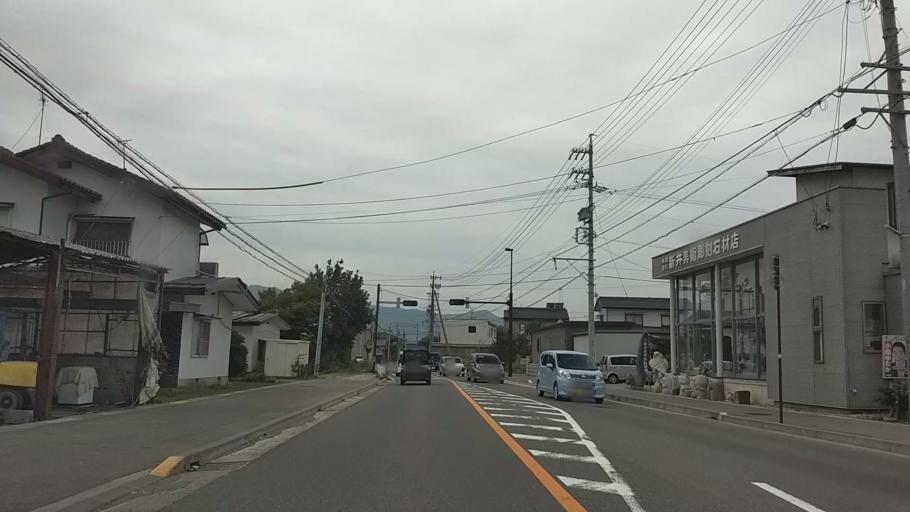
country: JP
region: Nagano
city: Nagano-shi
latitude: 36.5908
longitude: 138.1994
